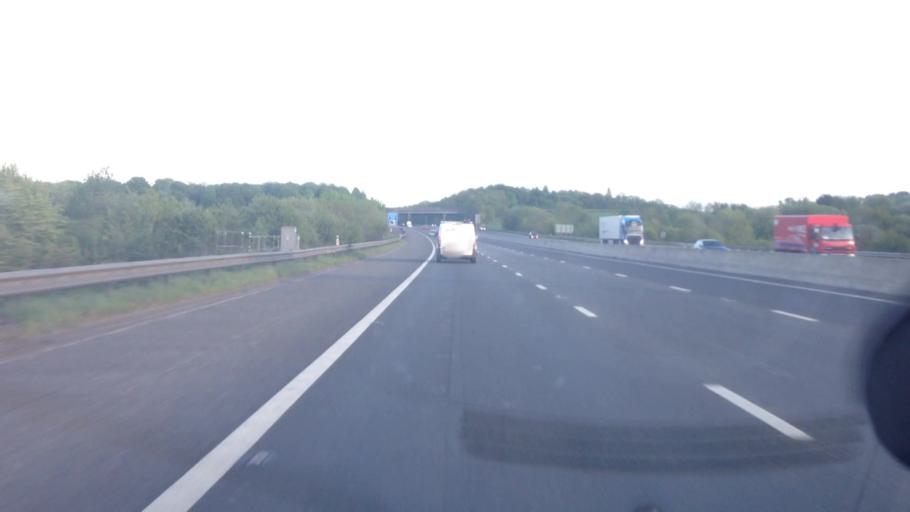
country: GB
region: England
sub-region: Sheffield
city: Chapletown
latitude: 53.4834
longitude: -1.4661
